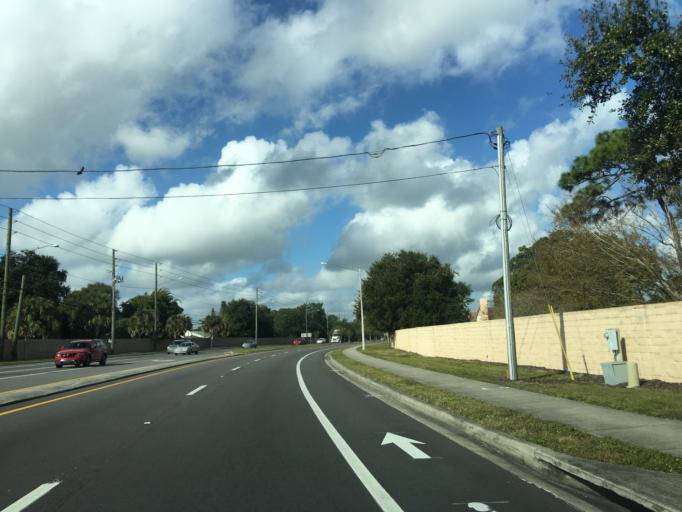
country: US
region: Florida
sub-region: Orange County
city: Azalea Park
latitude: 28.5102
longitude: -81.2798
